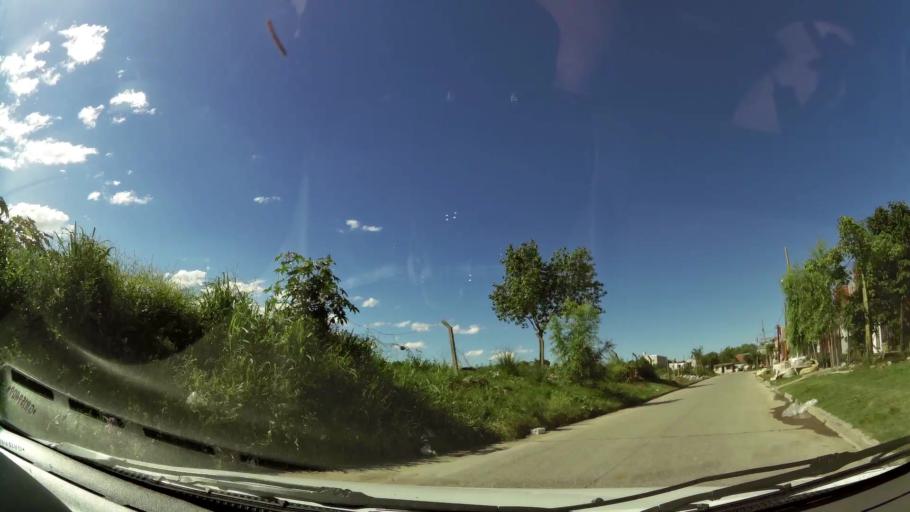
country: AR
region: Buenos Aires
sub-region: Partido de Tigre
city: Tigre
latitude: -34.5102
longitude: -58.5893
